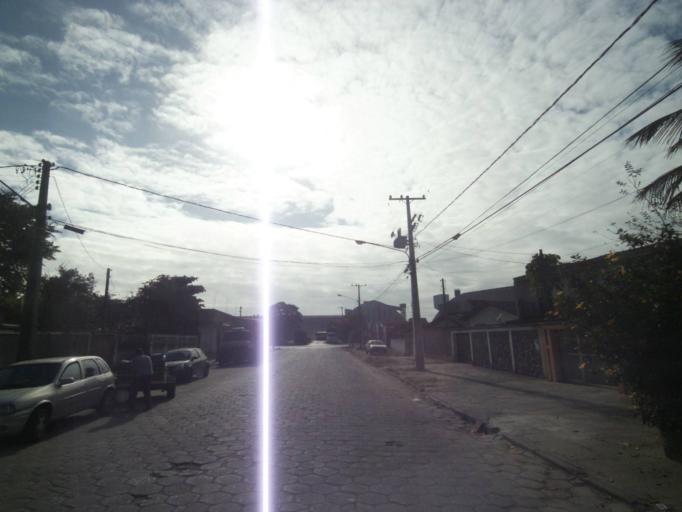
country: BR
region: Parana
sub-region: Paranagua
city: Paranagua
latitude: -25.5102
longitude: -48.5263
